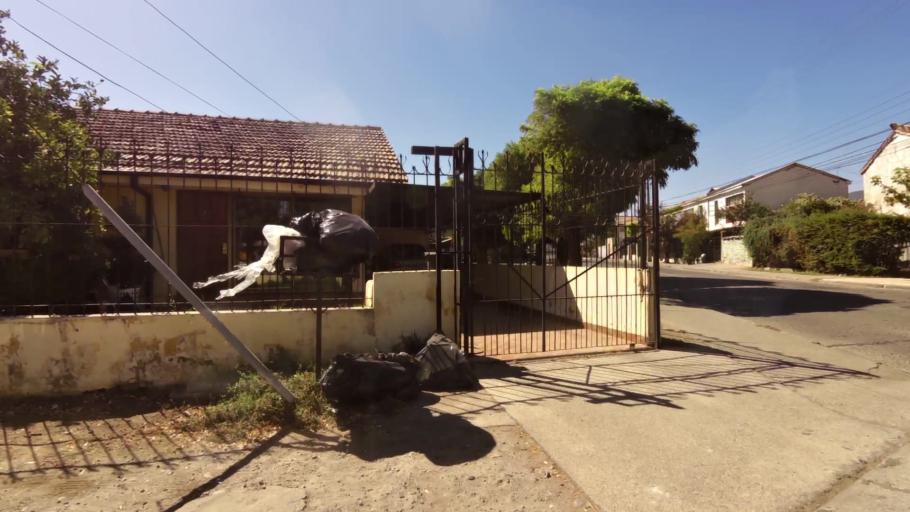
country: CL
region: O'Higgins
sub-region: Provincia de Cachapoal
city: Rancagua
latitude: -34.1805
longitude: -70.7384
